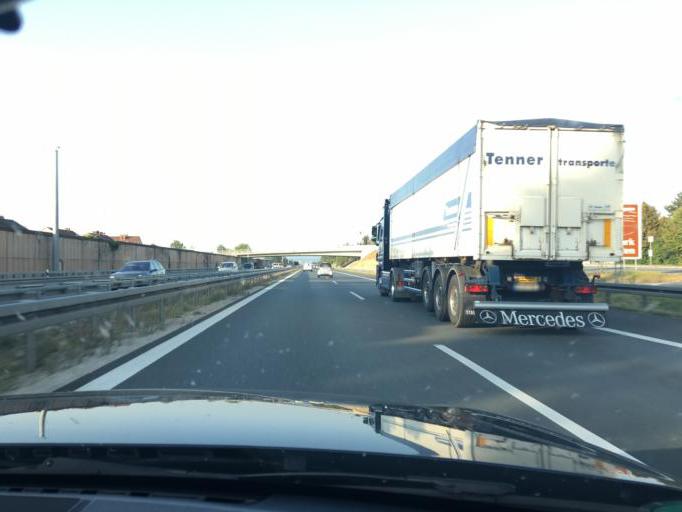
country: DE
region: Bavaria
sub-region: Regierungsbezirk Mittelfranken
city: Baiersdorf
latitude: 49.6565
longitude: 11.0357
